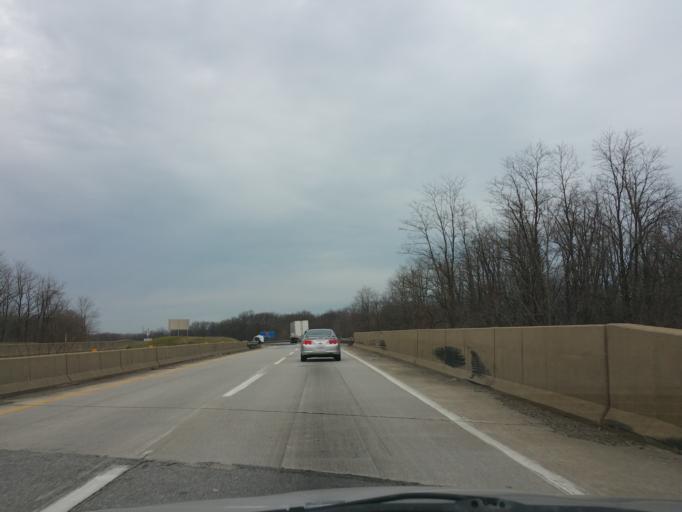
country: US
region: Indiana
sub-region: Porter County
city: Portage
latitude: 41.5840
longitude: -87.2008
